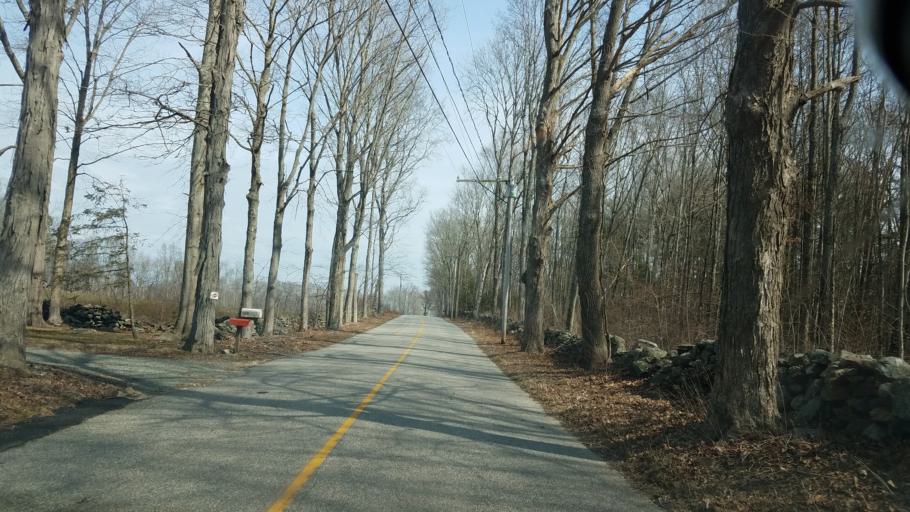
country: US
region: Connecticut
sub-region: New London County
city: Preston City
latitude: 41.5083
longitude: -71.9871
